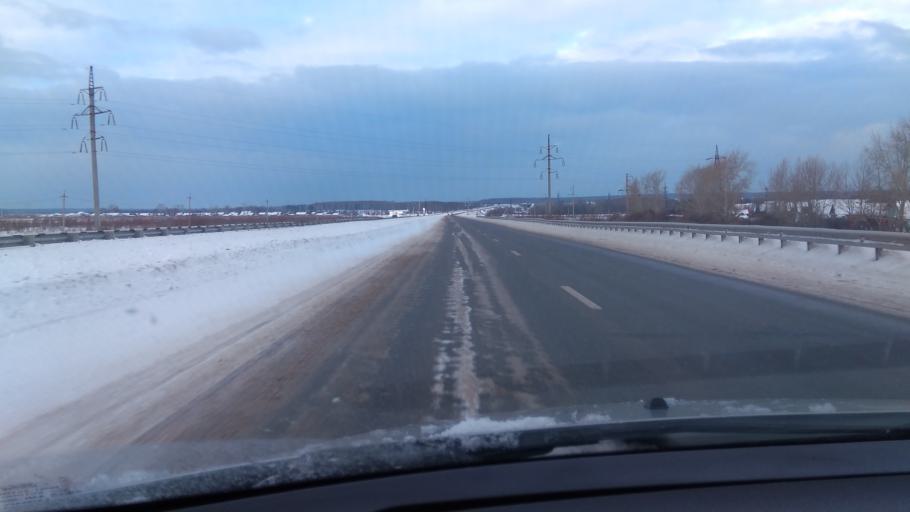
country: RU
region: Sverdlovsk
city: Tsementnyy
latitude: 57.4896
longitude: 60.1785
